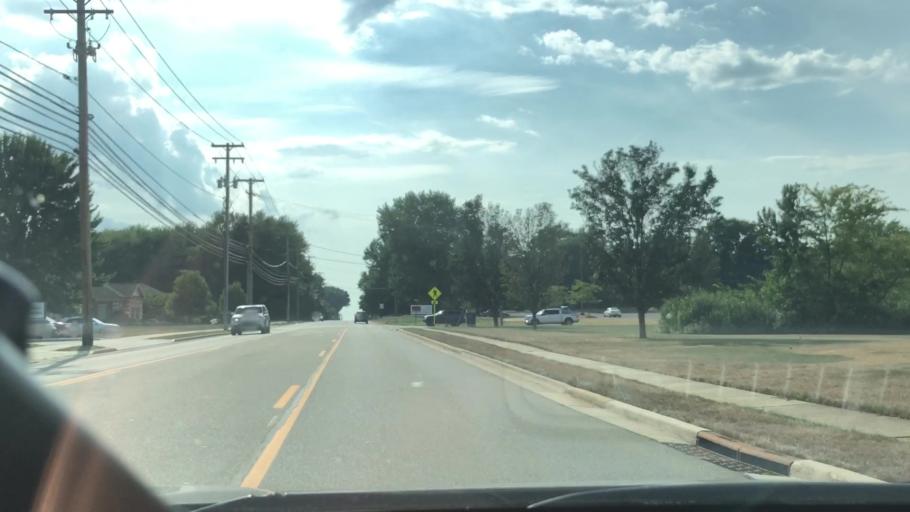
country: US
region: Ohio
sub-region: Summit County
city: Green
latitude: 40.9596
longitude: -81.4760
